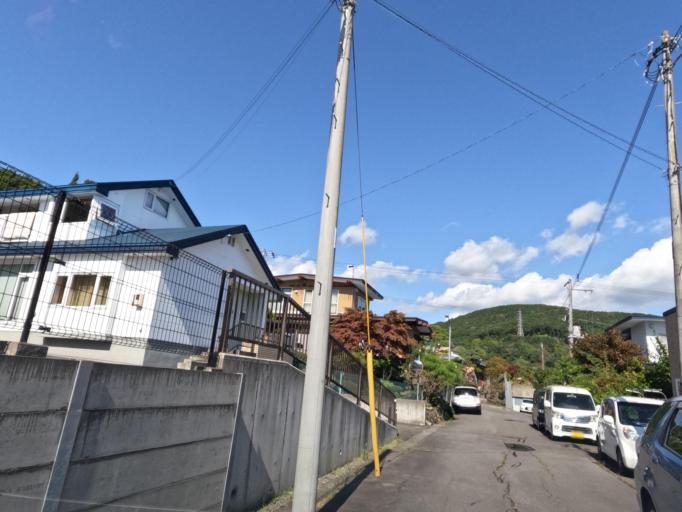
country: JP
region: Hokkaido
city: Muroran
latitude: 42.3702
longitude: 141.0258
